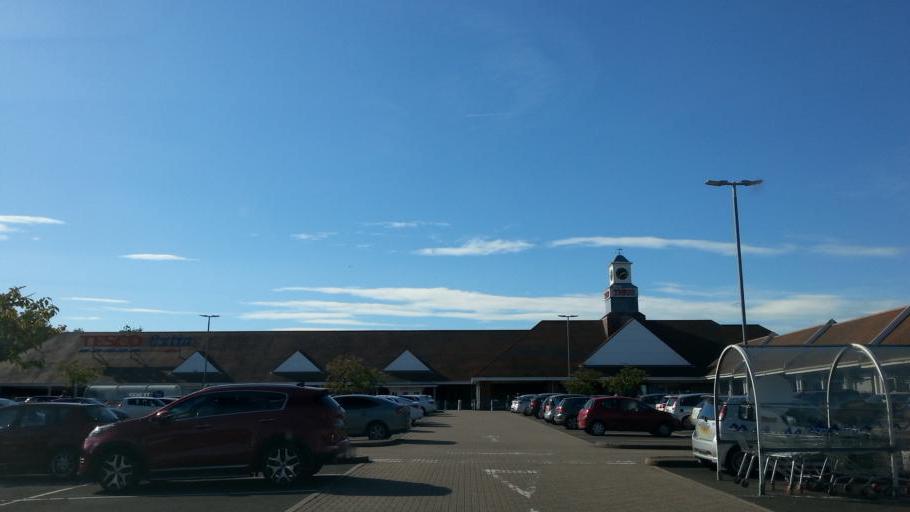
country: GB
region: England
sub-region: Shropshire
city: Hadley
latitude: 52.6896
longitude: -2.4912
